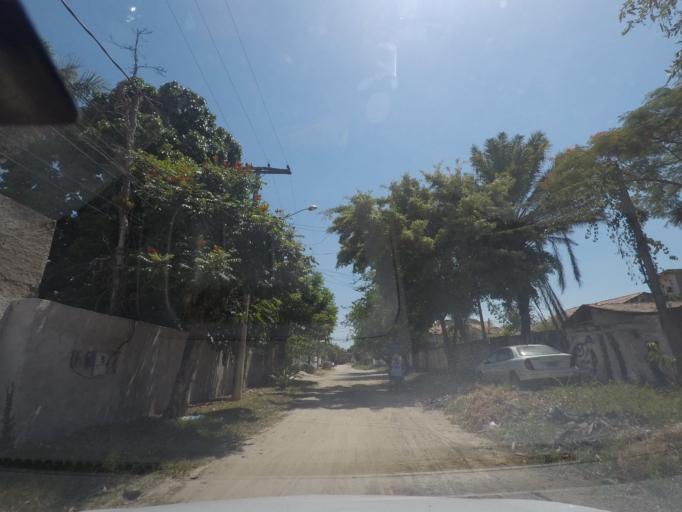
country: BR
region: Rio de Janeiro
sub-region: Niteroi
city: Niteroi
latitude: -22.9368
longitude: -43.0184
